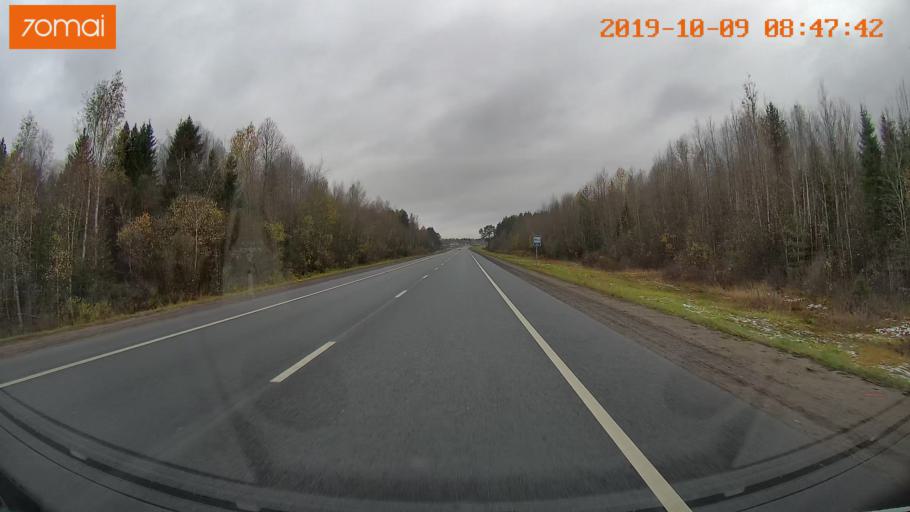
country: RU
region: Vologda
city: Vologda
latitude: 59.0672
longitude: 40.0407
